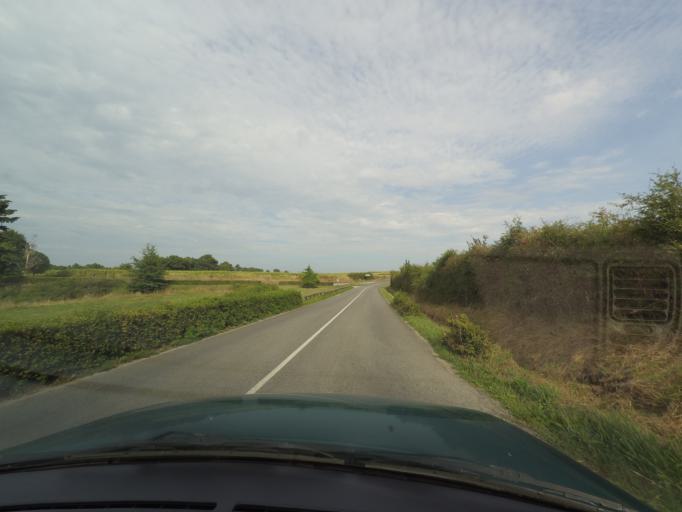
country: FR
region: Poitou-Charentes
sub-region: Departement de la Charente
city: Etagnac
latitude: 45.8496
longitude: 0.7717
